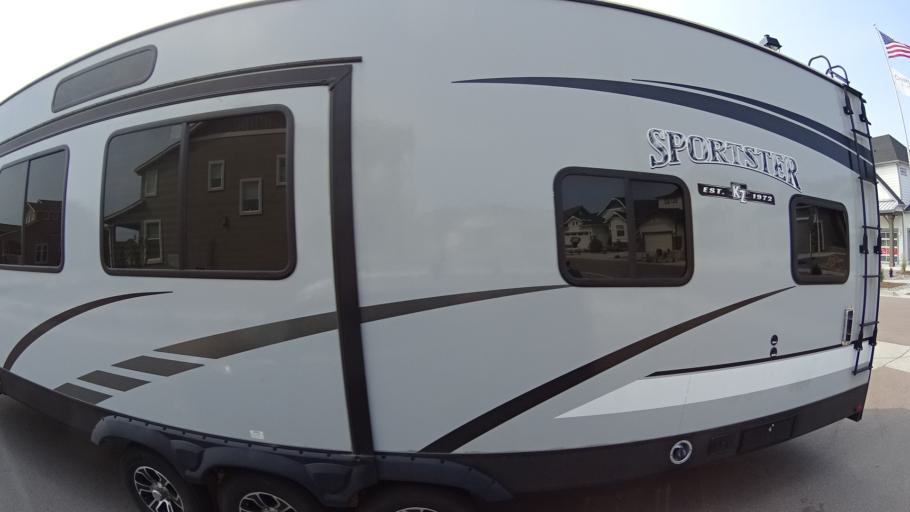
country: US
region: Colorado
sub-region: El Paso County
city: Black Forest
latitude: 38.9725
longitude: -104.7246
